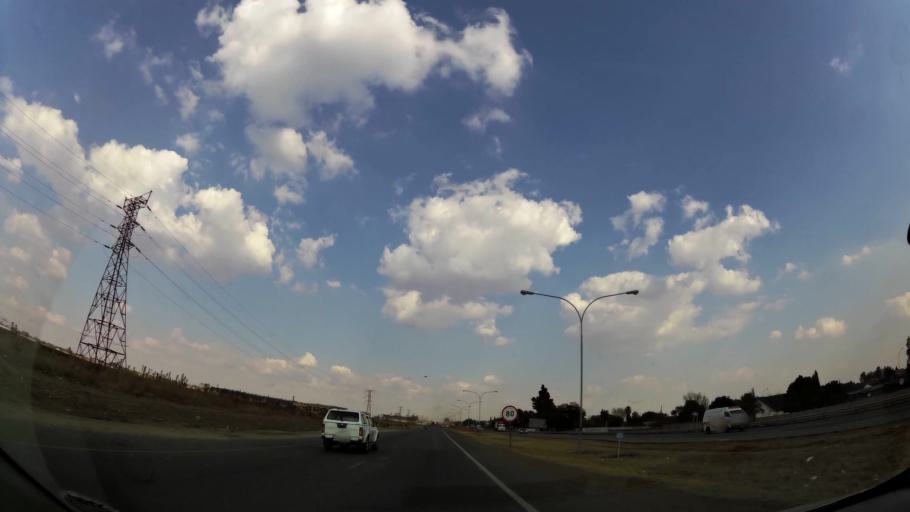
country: ZA
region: Gauteng
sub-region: Ekurhuleni Metropolitan Municipality
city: Brakpan
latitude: -26.2596
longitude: 28.3230
